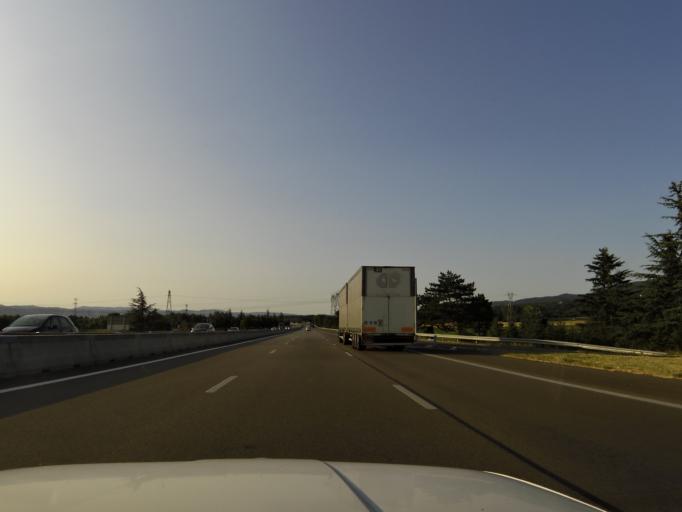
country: FR
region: Rhone-Alpes
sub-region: Departement de la Drome
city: Saulce-sur-Rhone
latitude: 44.6700
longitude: 4.7973
